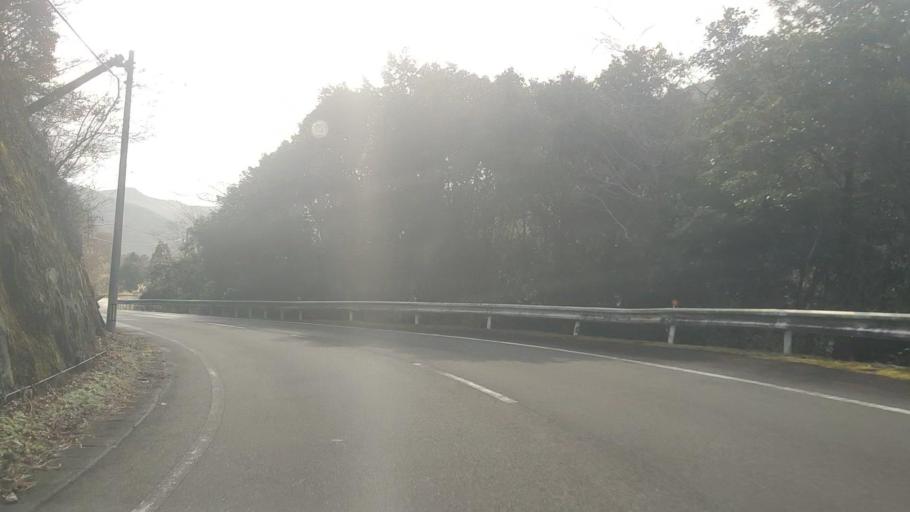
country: JP
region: Kumamoto
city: Hitoyoshi
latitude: 32.3220
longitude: 130.8397
